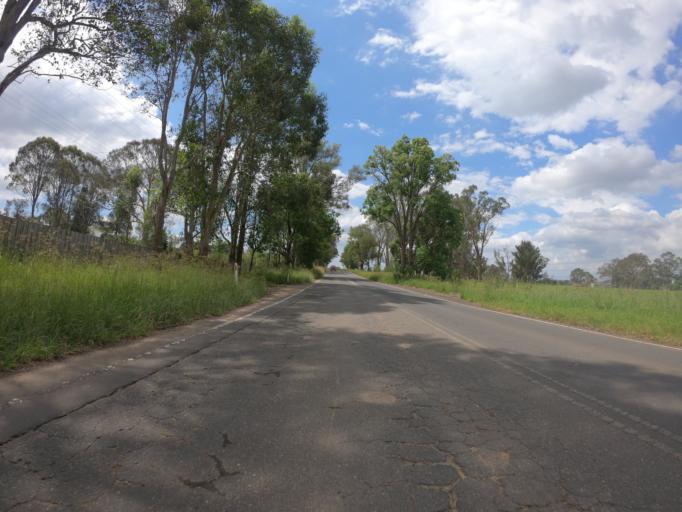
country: AU
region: New South Wales
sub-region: Penrith Municipality
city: Kingswood Park
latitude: -33.8277
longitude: 150.7593
